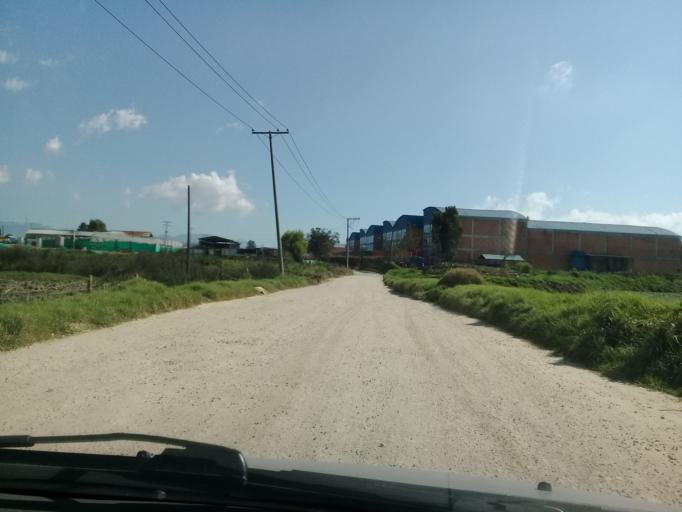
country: CO
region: Cundinamarca
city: Funza
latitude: 4.7274
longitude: -74.1948
